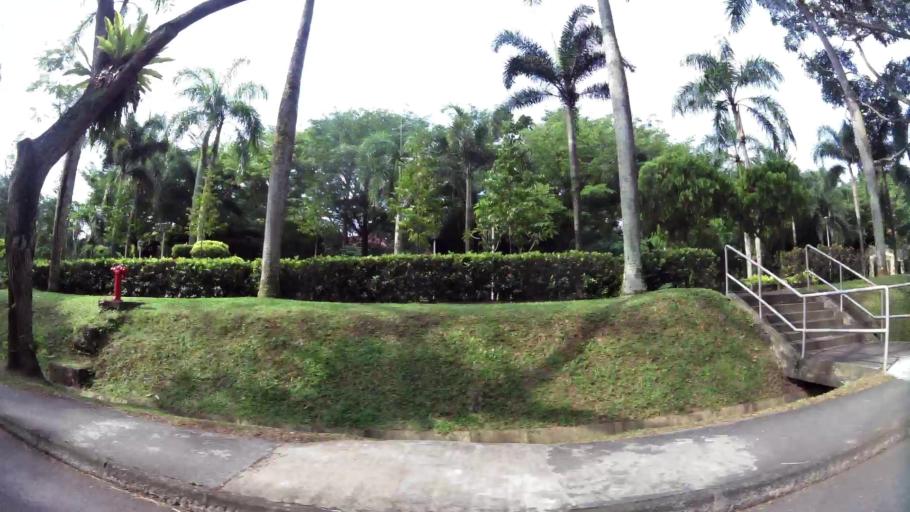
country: SG
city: Singapore
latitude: 1.2964
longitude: 103.7979
